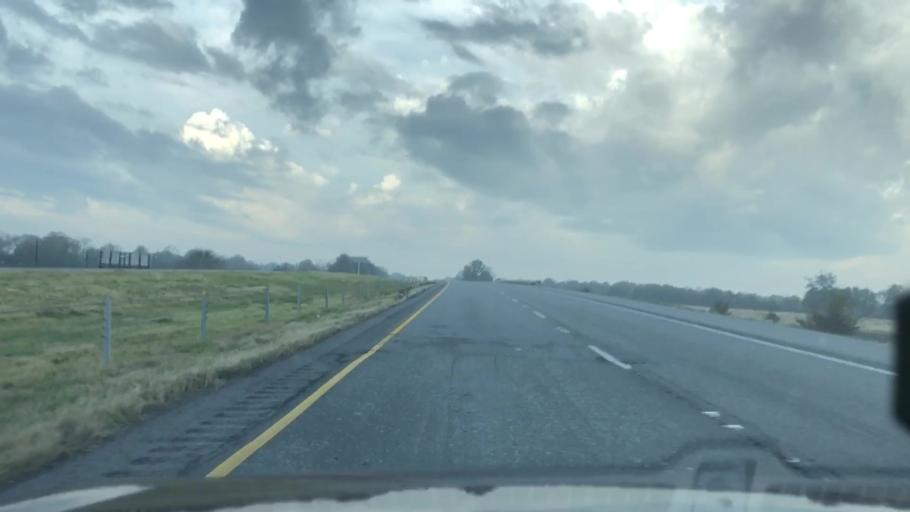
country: US
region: Louisiana
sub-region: Madison Parish
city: Tallulah
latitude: 32.4046
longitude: -91.2243
